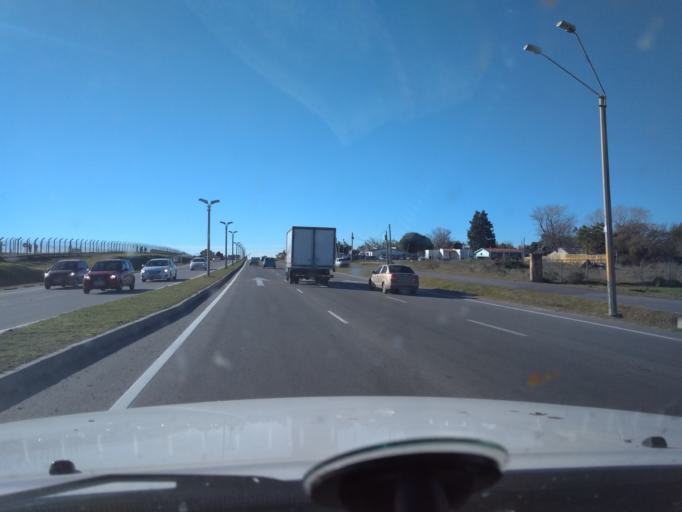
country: UY
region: Canelones
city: Colonia Nicolich
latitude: -34.8282
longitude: -56.0102
